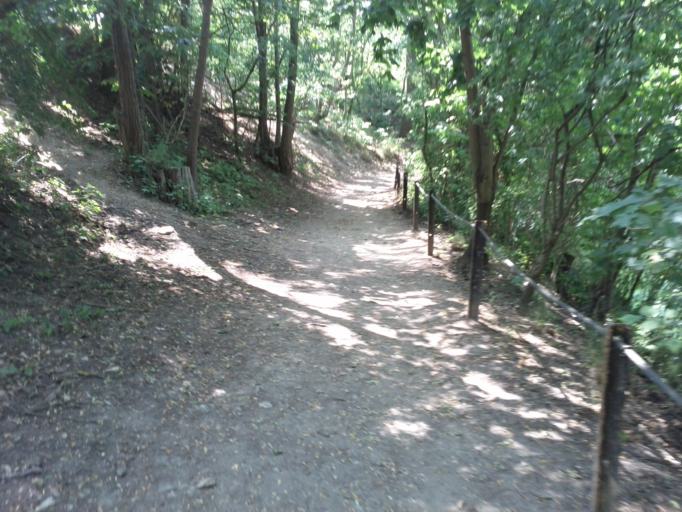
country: DE
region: Brandenburg
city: Woltersdorf
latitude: 52.4773
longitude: 13.7809
